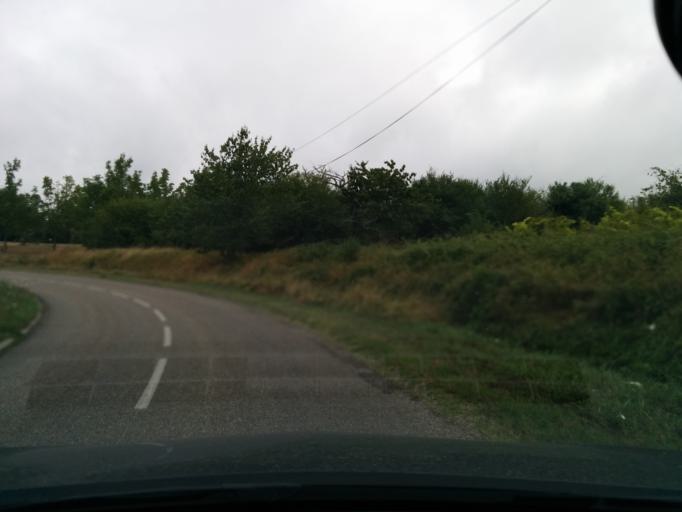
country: FR
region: Midi-Pyrenees
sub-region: Departement du Tarn-et-Garonne
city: Moissac
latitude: 44.1533
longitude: 1.0656
